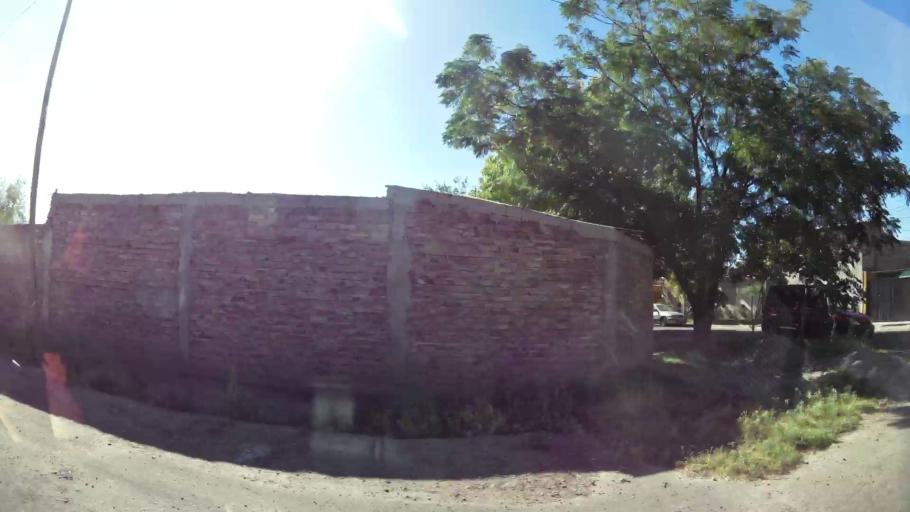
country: AR
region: Mendoza
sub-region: Departamento de Godoy Cruz
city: Godoy Cruz
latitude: -32.9279
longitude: -68.8636
